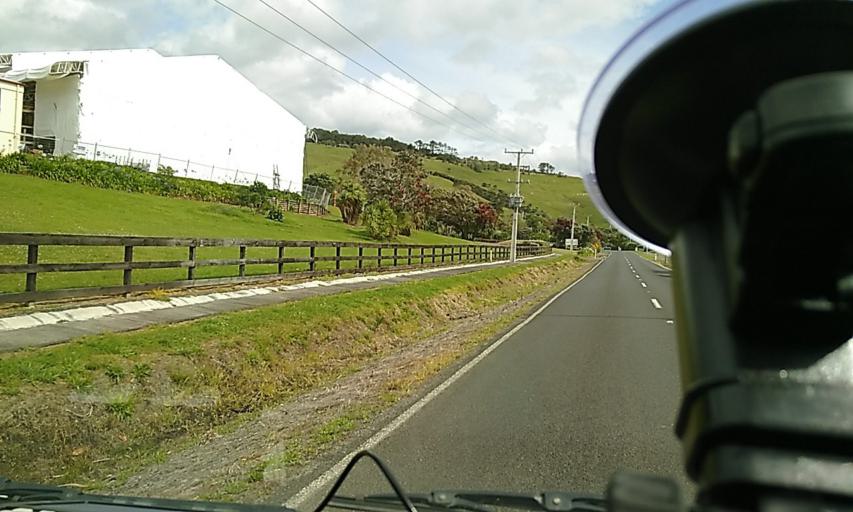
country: NZ
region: Northland
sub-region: Far North District
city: Ahipara
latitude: -35.5283
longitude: 173.3898
